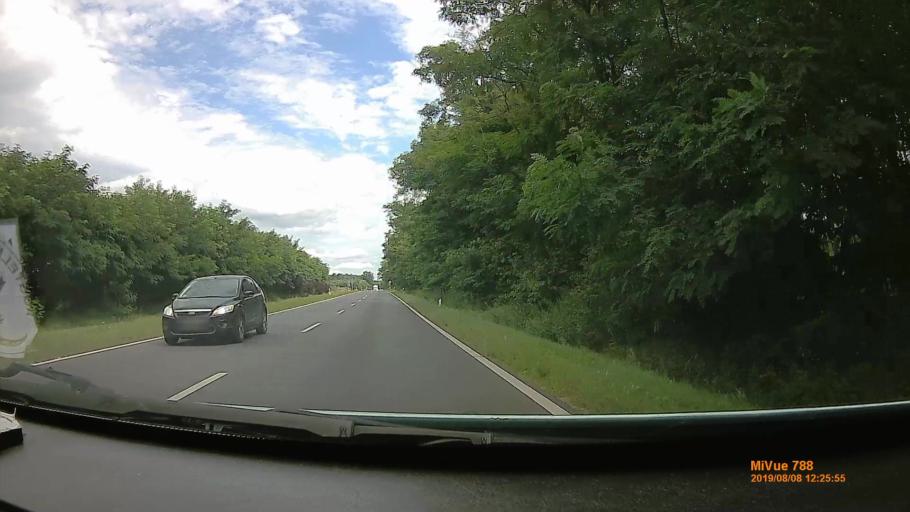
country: HU
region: Szabolcs-Szatmar-Bereg
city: Nyirbogat
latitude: 47.8139
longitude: 22.0795
